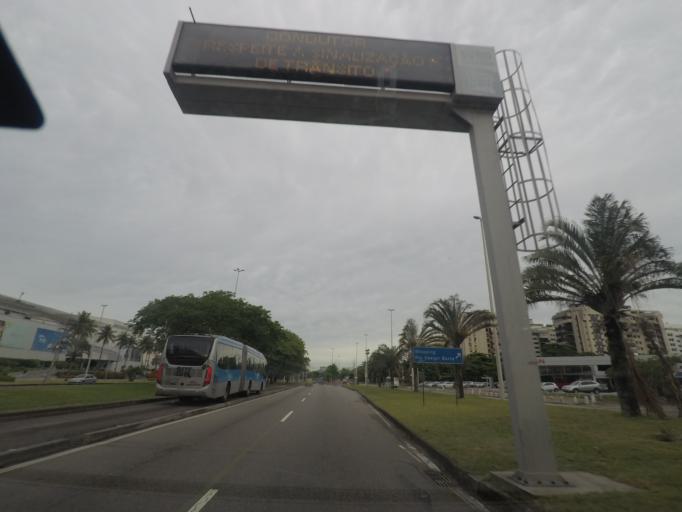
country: BR
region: Rio de Janeiro
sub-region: Nilopolis
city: Nilopolis
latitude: -23.0003
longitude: -43.3847
